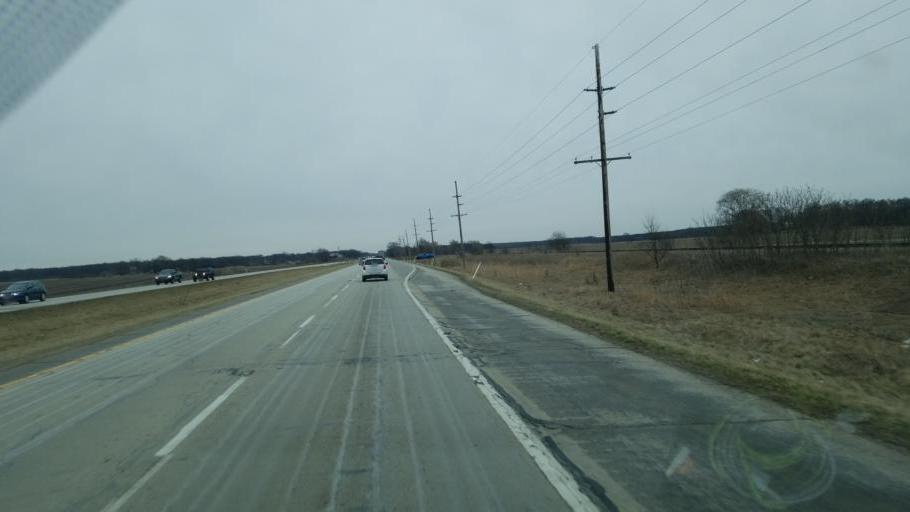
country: US
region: Indiana
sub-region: Starke County
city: Koontz Lake
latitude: 41.3758
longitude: -86.5362
